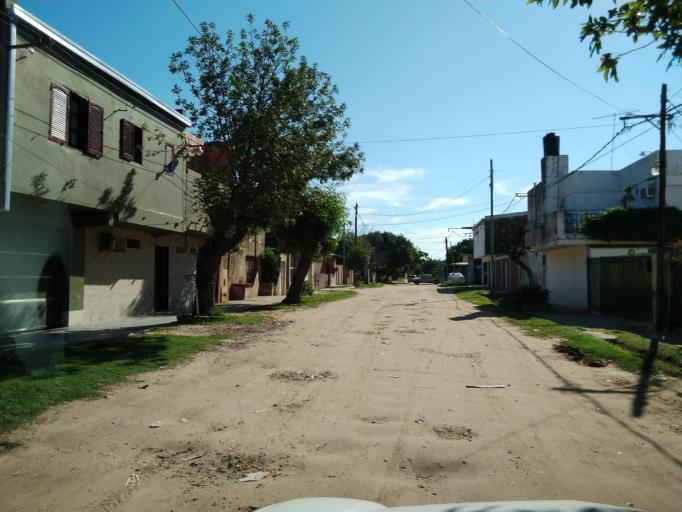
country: AR
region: Corrientes
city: Corrientes
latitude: -27.4855
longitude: -58.8074
